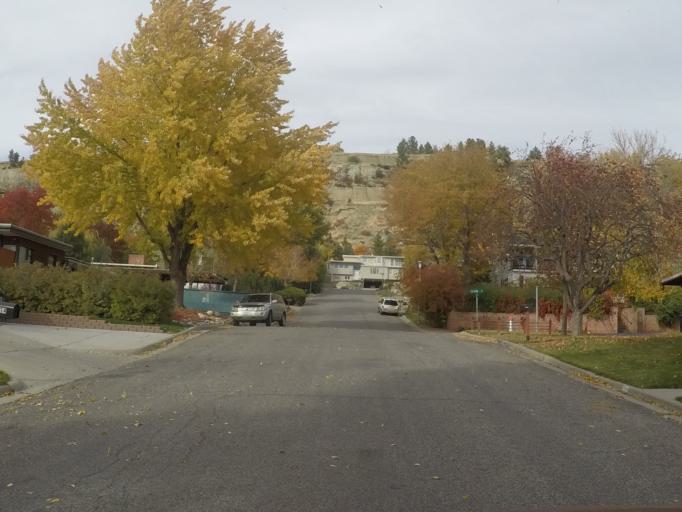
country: US
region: Montana
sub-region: Yellowstone County
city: Billings
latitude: 45.7999
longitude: -108.5539
